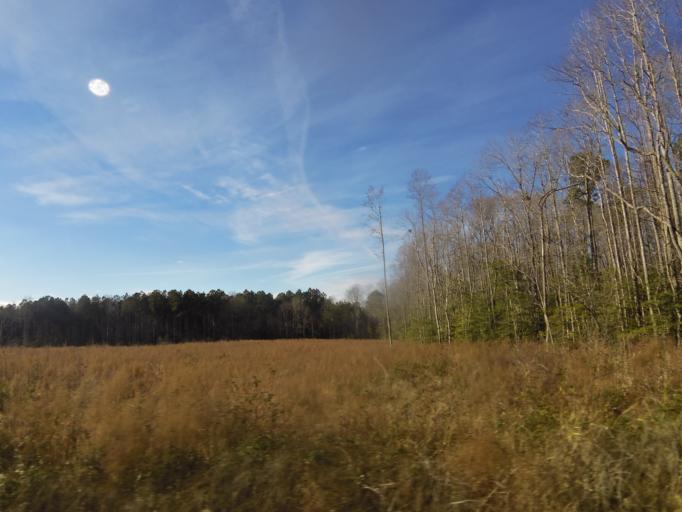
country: US
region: Virginia
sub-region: Isle of Wight County
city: Isle of Wight
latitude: 36.8751
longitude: -76.7291
